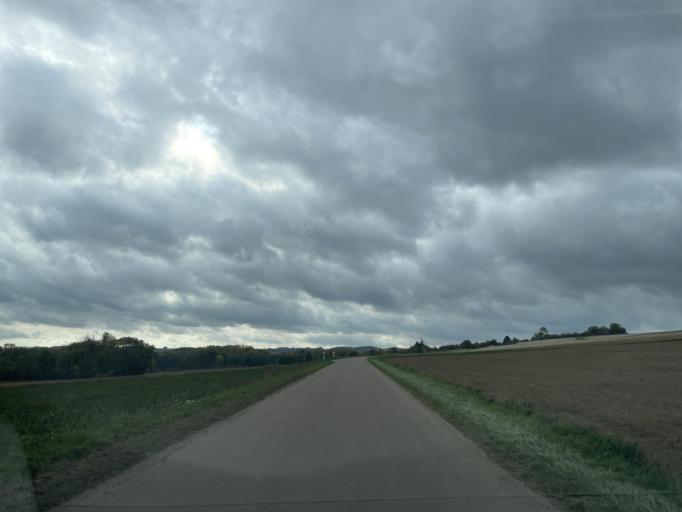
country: FR
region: Bourgogne
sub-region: Departement de l'Yonne
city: Aillant-sur-Tholon
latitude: 47.8302
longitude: 3.3497
